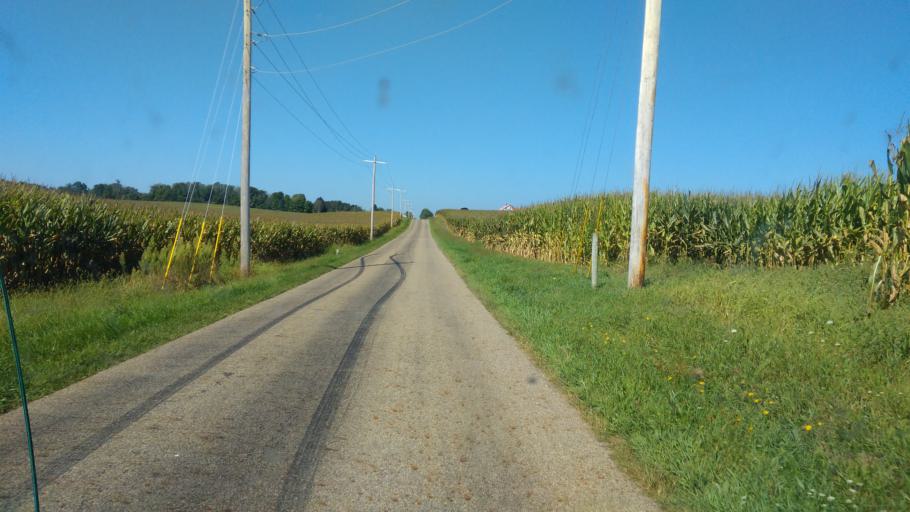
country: US
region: Ohio
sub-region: Knox County
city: Fredericktown
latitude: 40.4597
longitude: -82.5036
